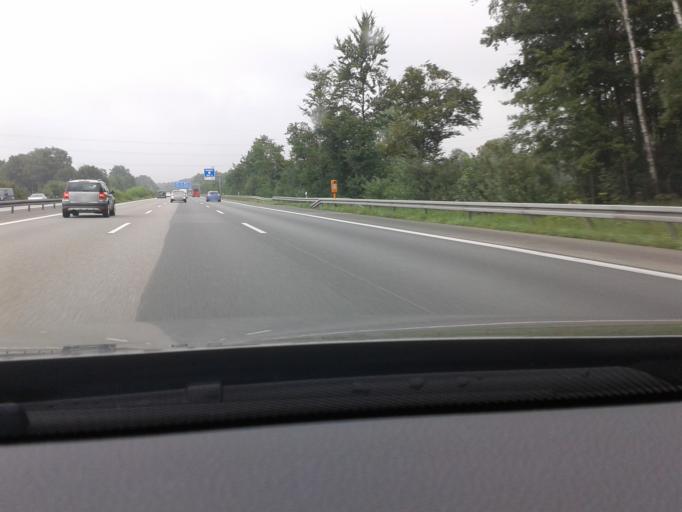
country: DE
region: North Rhine-Westphalia
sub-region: Regierungsbezirk Detmold
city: Verl
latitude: 51.9179
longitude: 8.5199
